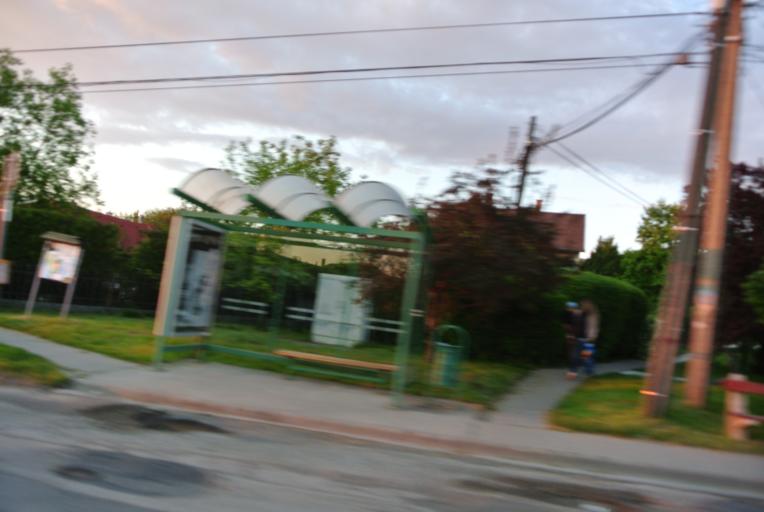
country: HU
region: Pest
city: Telki
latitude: 47.5488
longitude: 18.8246
